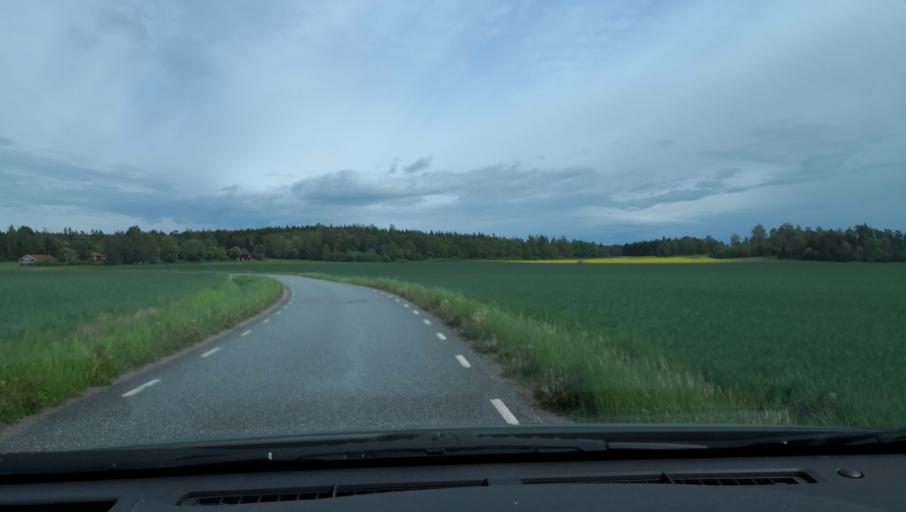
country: SE
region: Uppsala
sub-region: Enkopings Kommun
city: Orsundsbro
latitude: 59.7036
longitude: 17.4146
